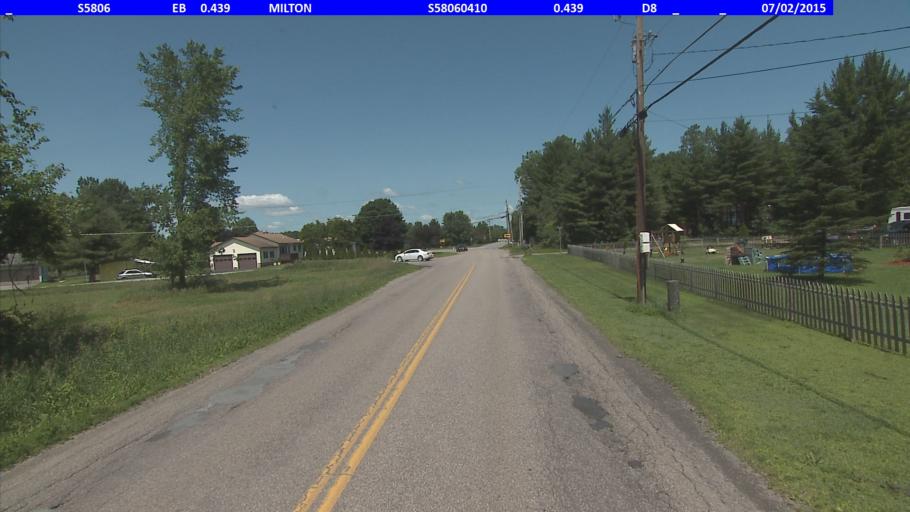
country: US
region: Vermont
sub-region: Chittenden County
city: Milton
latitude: 44.6569
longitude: -73.1199
